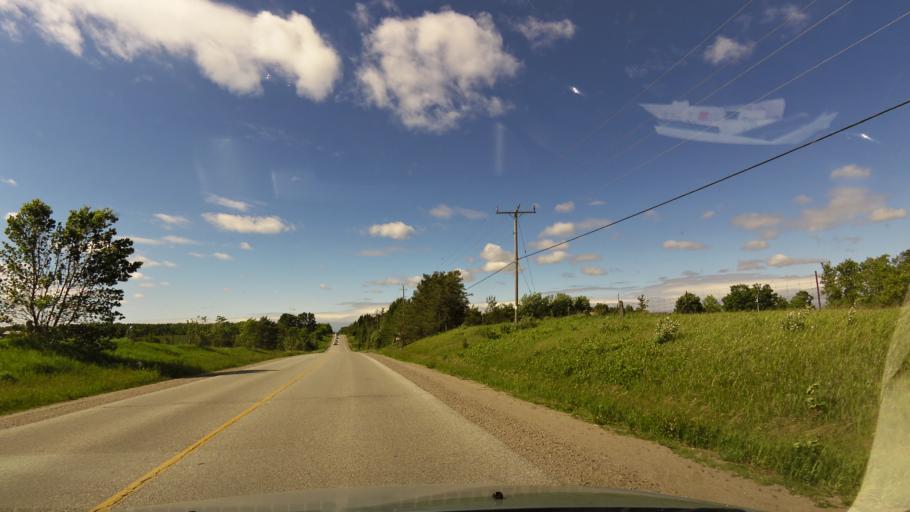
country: CA
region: Ontario
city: Bradford West Gwillimbury
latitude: 44.1391
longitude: -79.6100
